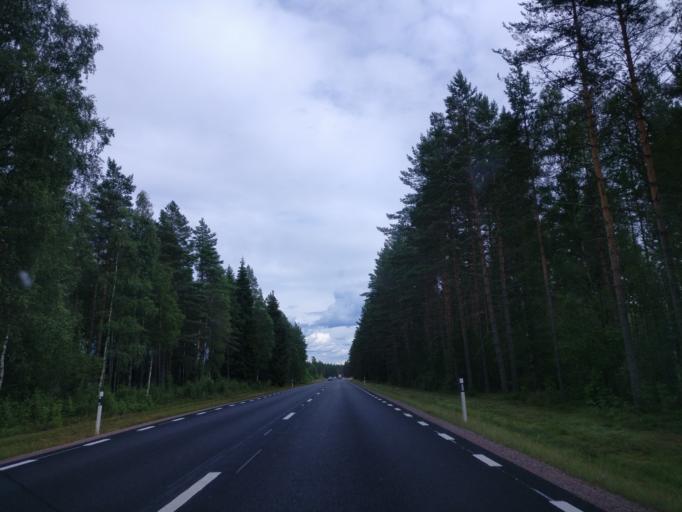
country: SE
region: Vaermland
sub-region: Hagfors Kommun
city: Hagfors
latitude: 60.0508
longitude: 13.5653
